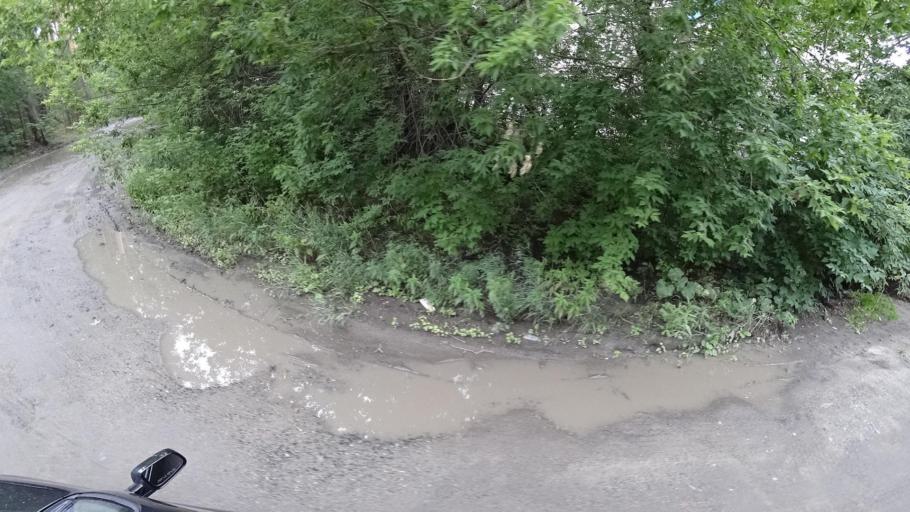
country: RU
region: Sverdlovsk
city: Kamyshlov
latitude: 56.8346
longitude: 62.7345
